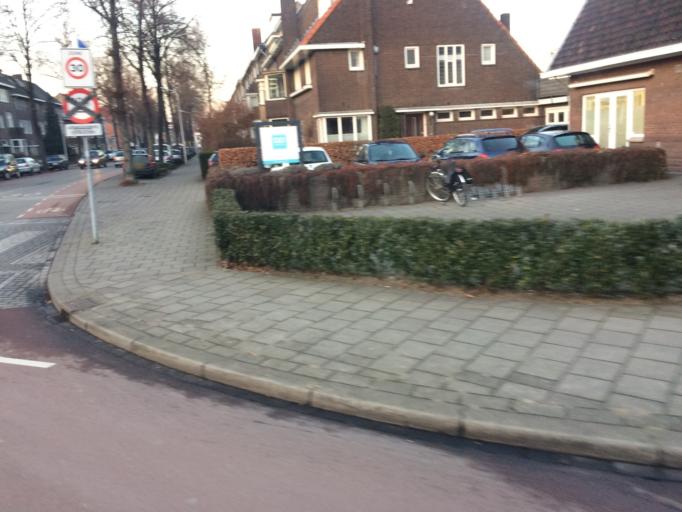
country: NL
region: Limburg
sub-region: Gemeente Maastricht
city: Heer
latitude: 50.8488
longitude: 5.7187
